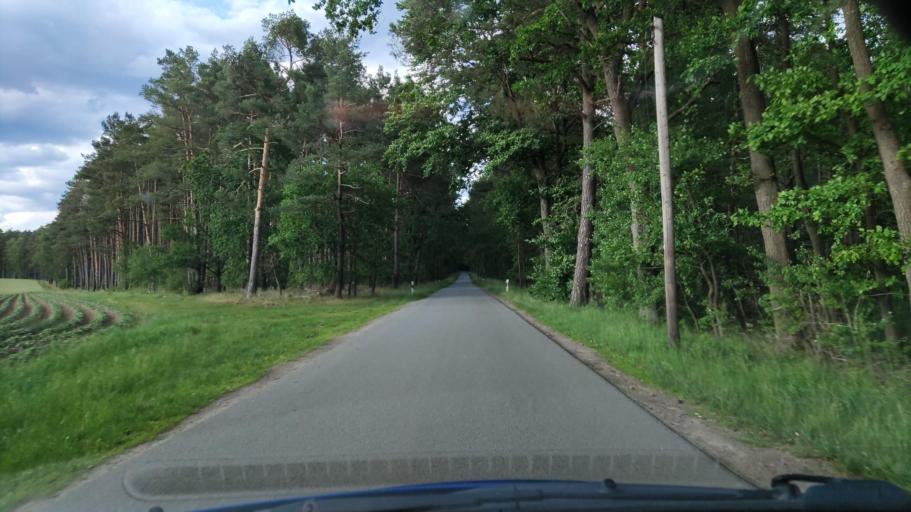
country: DE
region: Lower Saxony
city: Schnega
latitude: 52.9191
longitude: 10.8521
